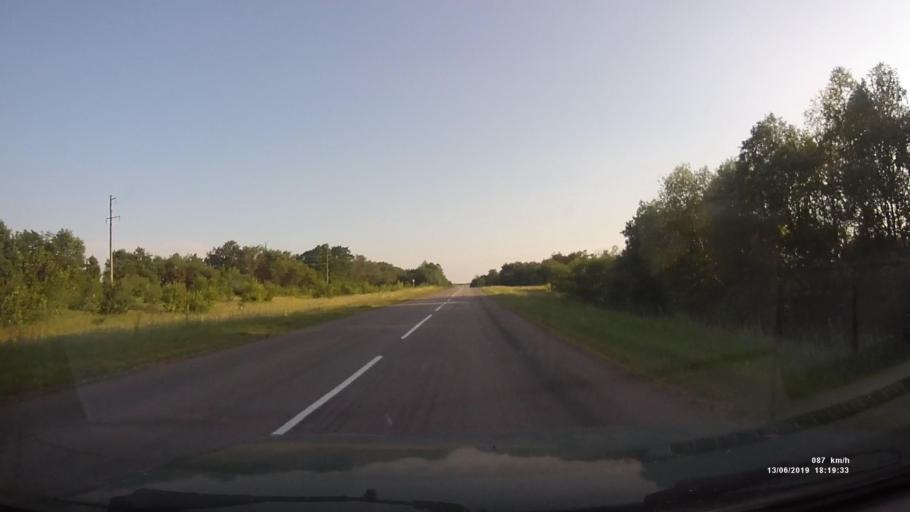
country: RU
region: Rostov
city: Kazanskaya
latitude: 49.8946
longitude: 41.3056
